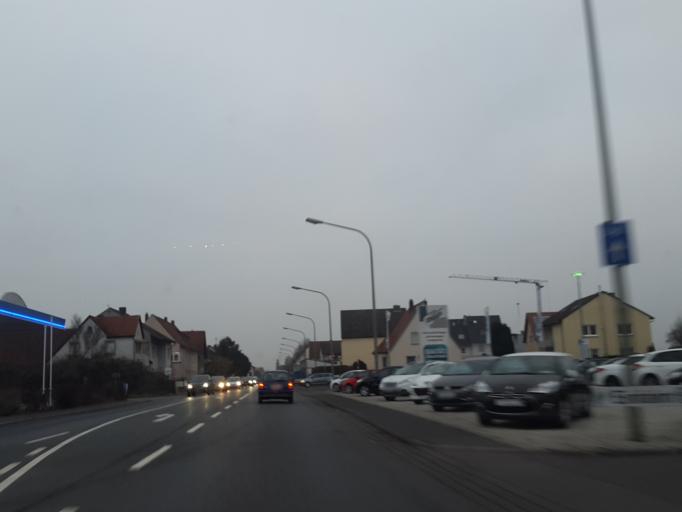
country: DE
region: Bavaria
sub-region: Regierungsbezirk Unterfranken
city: Kleinostheim
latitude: 49.9951
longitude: 9.0689
